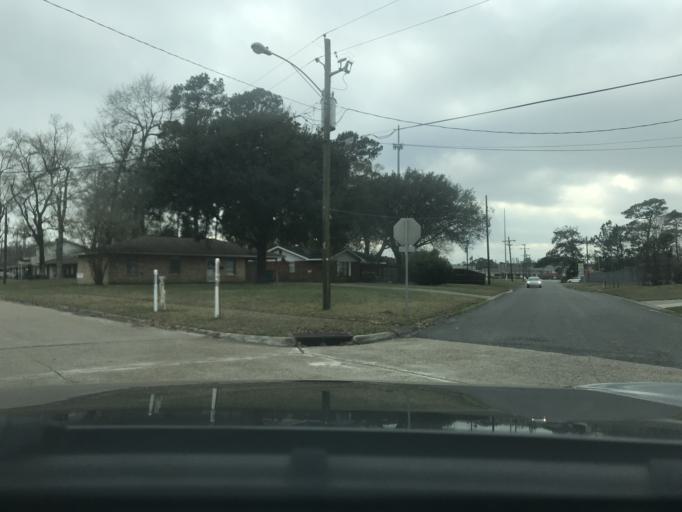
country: US
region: Louisiana
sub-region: Calcasieu Parish
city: Westlake
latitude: 30.2547
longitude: -93.2555
